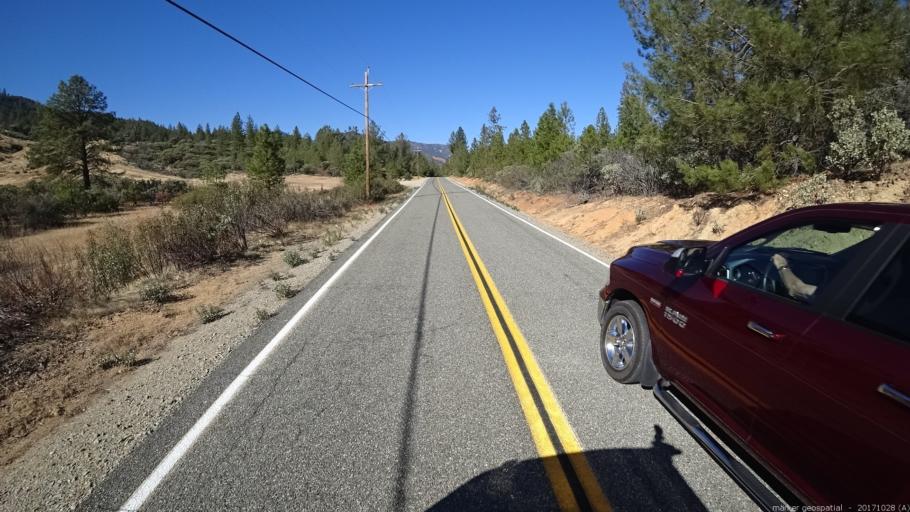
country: US
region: California
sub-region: Shasta County
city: Shasta
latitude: 40.6446
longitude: -122.4582
